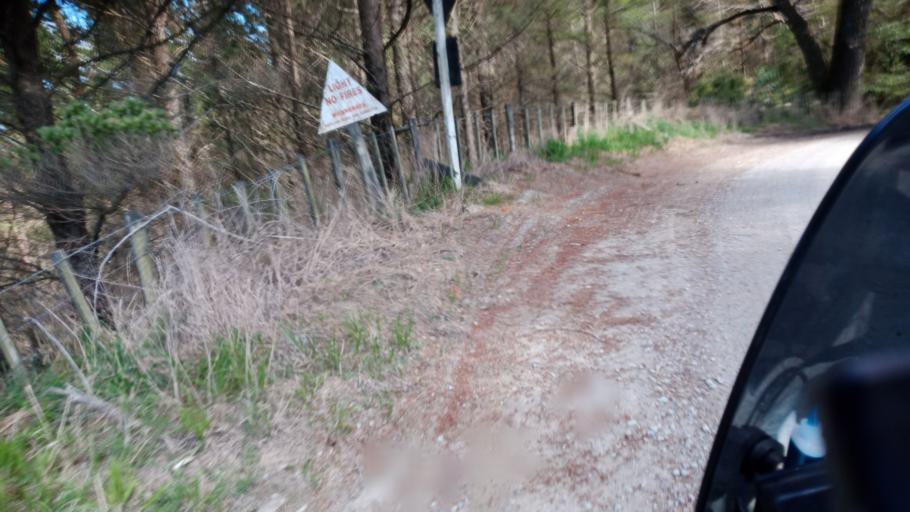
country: NZ
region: Gisborne
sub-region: Gisborne District
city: Gisborne
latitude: -38.8120
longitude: 177.7655
